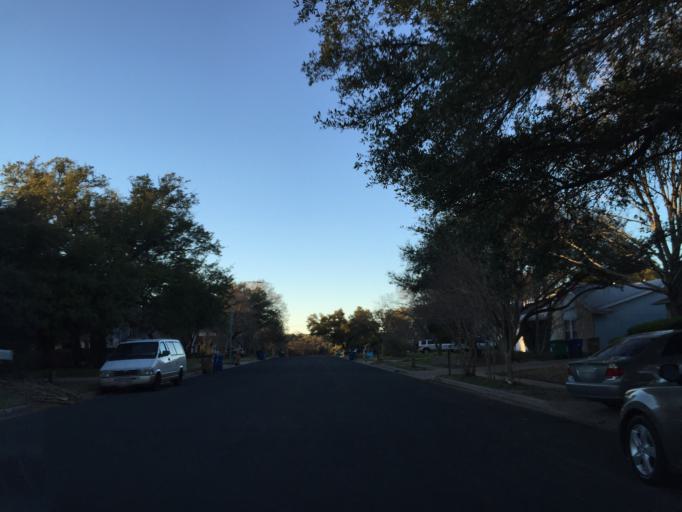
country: US
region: Texas
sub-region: Williamson County
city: Jollyville
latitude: 30.4291
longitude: -97.7791
